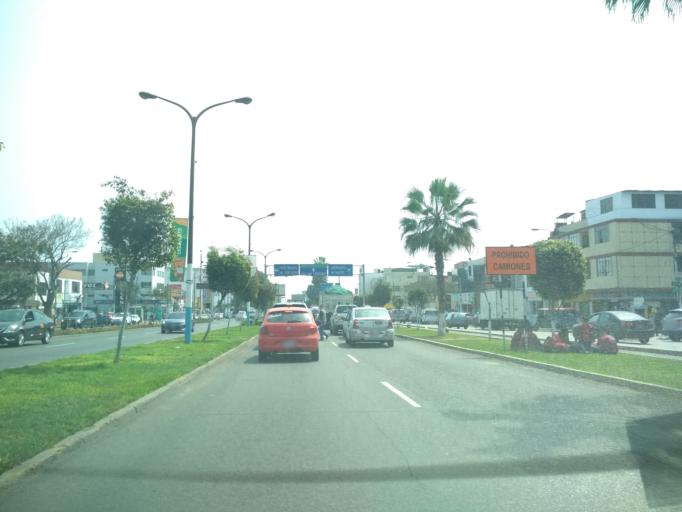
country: PE
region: Callao
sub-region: Callao
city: Callao
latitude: -12.0527
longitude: -77.0946
